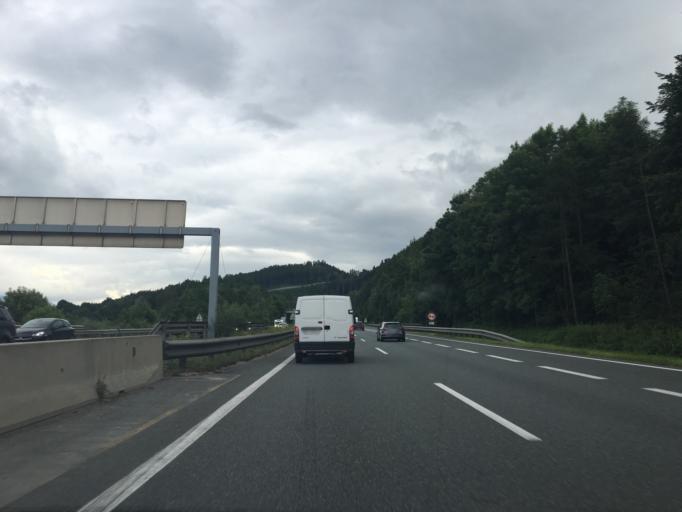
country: AT
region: Tyrol
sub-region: Politischer Bezirk Innsbruck Land
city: Ampass
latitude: 47.2616
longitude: 11.4439
